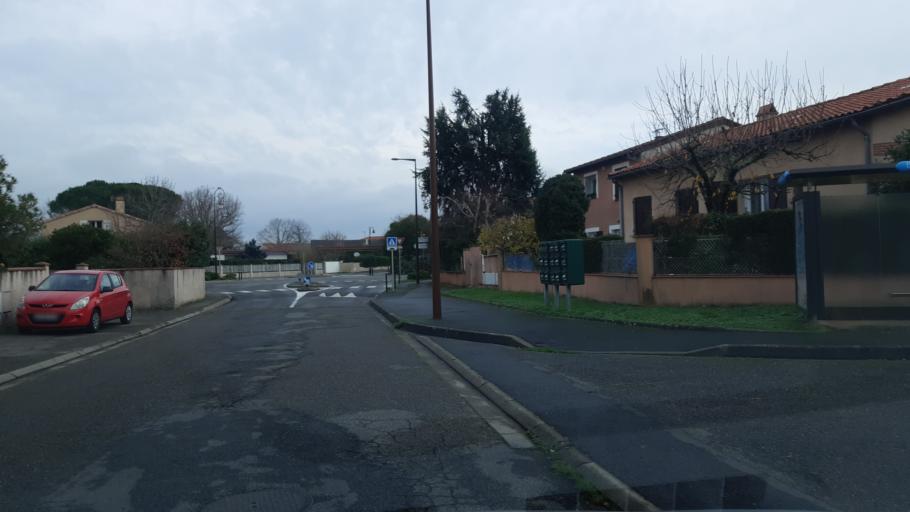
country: FR
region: Midi-Pyrenees
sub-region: Departement de la Haute-Garonne
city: Pibrac
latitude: 43.6132
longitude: 1.2850
